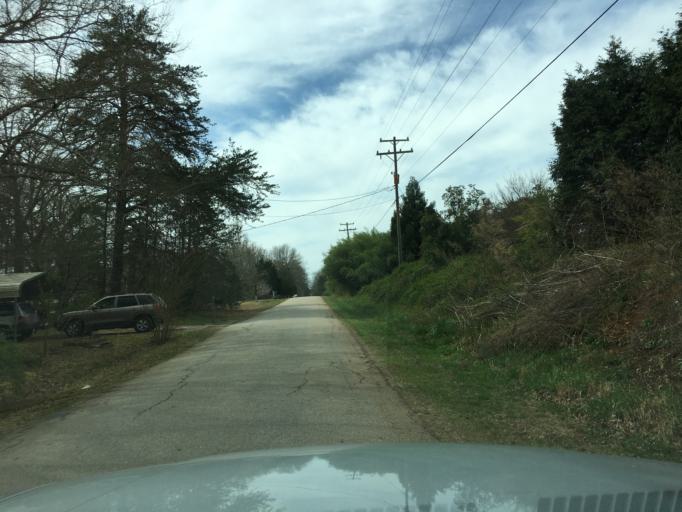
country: US
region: South Carolina
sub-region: Spartanburg County
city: Wellford
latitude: 34.8962
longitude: -82.0632
